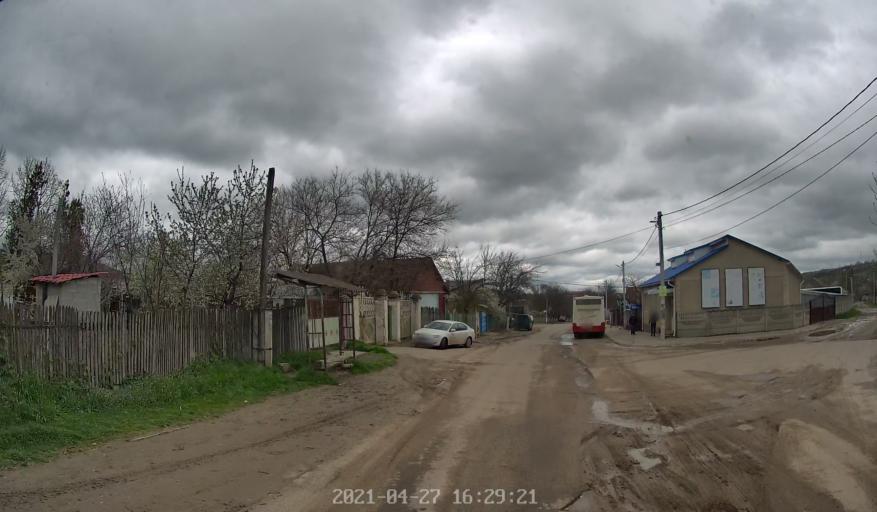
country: MD
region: Chisinau
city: Singera
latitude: 46.9679
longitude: 29.0503
